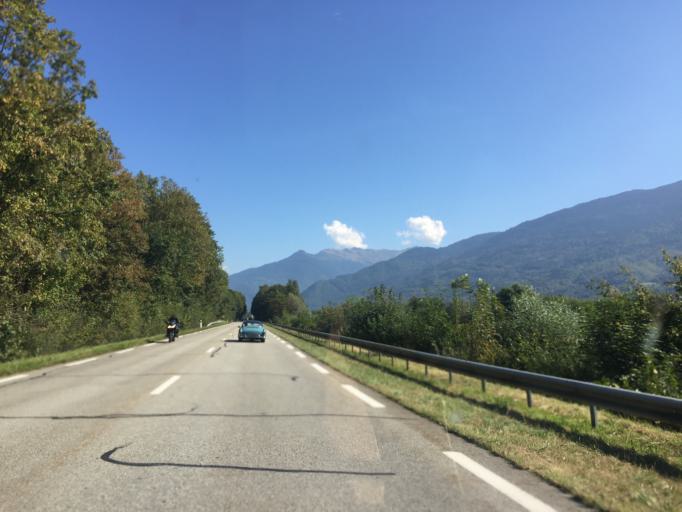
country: FR
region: Rhone-Alpes
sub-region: Departement de la Savoie
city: Sainte-Helene-sur-Isere
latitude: 45.6195
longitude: 6.3064
